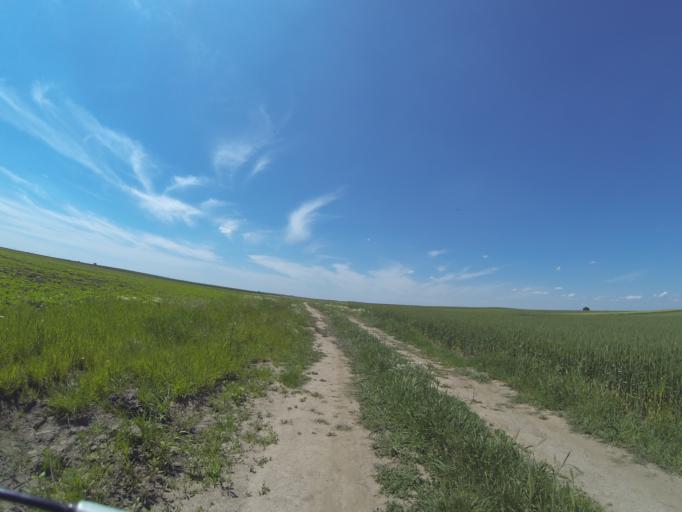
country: RO
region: Dolj
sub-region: Comuna Leu
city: Leu
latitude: 44.2157
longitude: 24.0212
